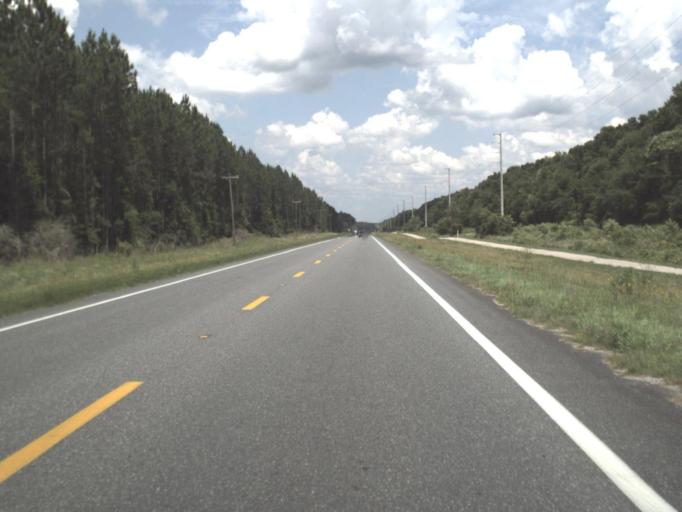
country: US
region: Florida
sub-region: Alachua County
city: High Springs
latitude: 29.9527
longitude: -82.8185
